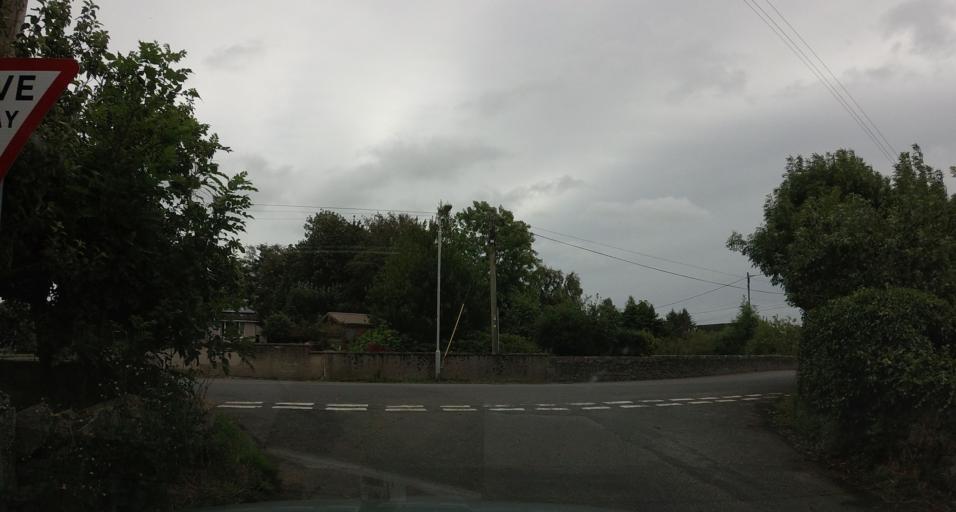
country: GB
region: Scotland
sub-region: Aberdeenshire
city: Kemnay
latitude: 57.2178
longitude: -2.4609
